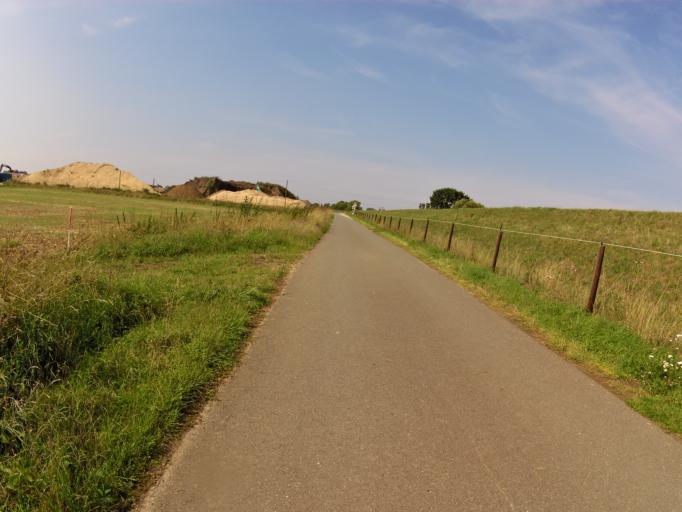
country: DE
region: Lower Saxony
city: Riede
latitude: 53.0037
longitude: 8.9056
